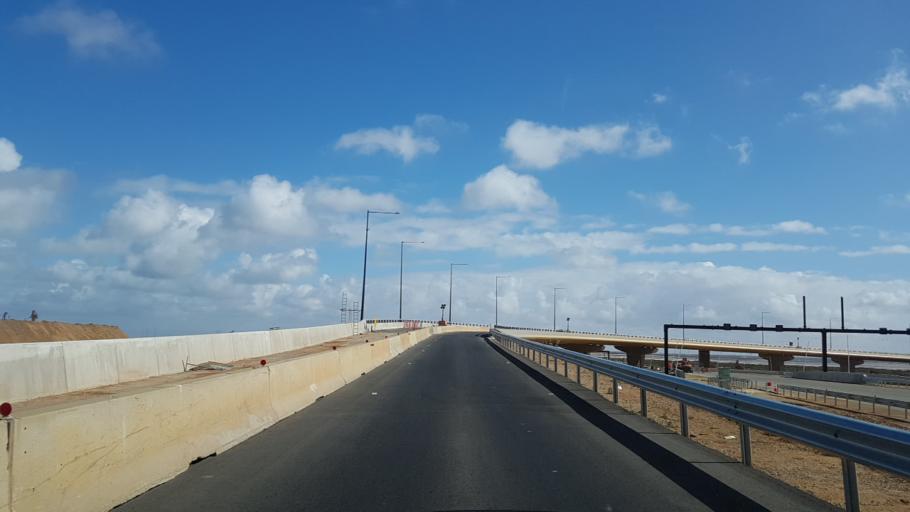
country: AU
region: South Australia
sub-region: Port Adelaide Enfield
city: Blair Athol
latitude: -34.8315
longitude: 138.5621
